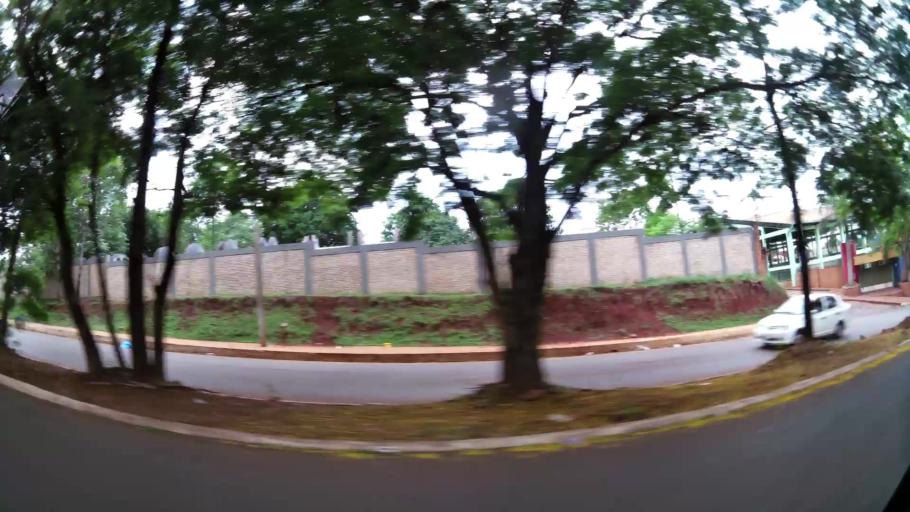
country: PY
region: Alto Parana
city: Presidente Franco
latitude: -25.5217
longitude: -54.6449
